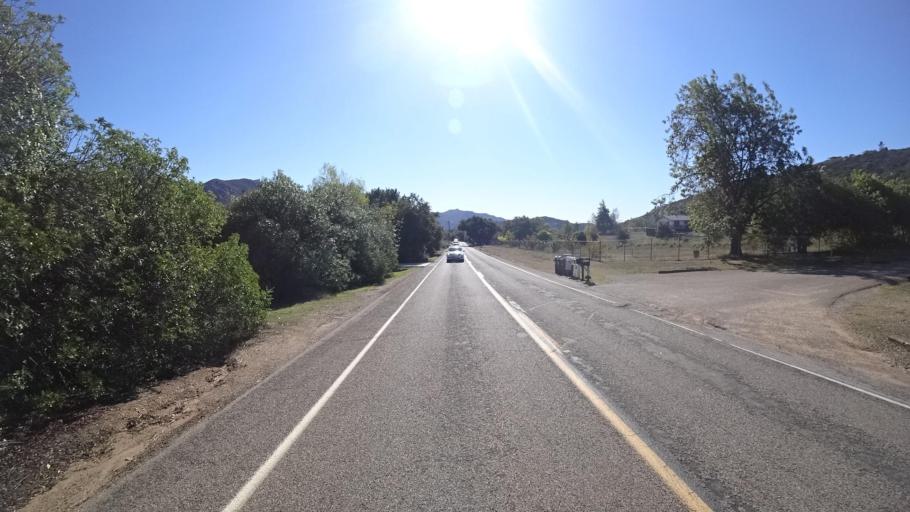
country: US
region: California
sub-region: San Diego County
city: Jamul
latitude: 32.7285
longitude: -116.8185
